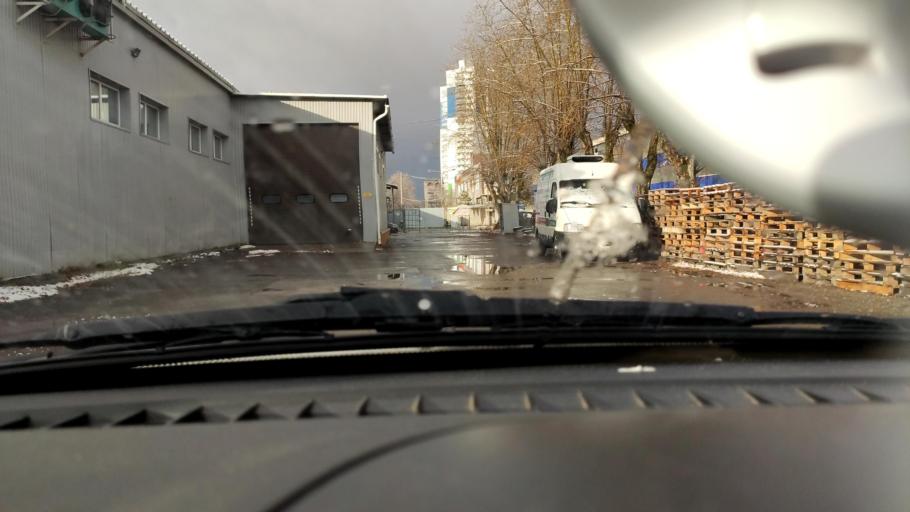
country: RU
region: Perm
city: Perm
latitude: 57.9700
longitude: 56.2365
